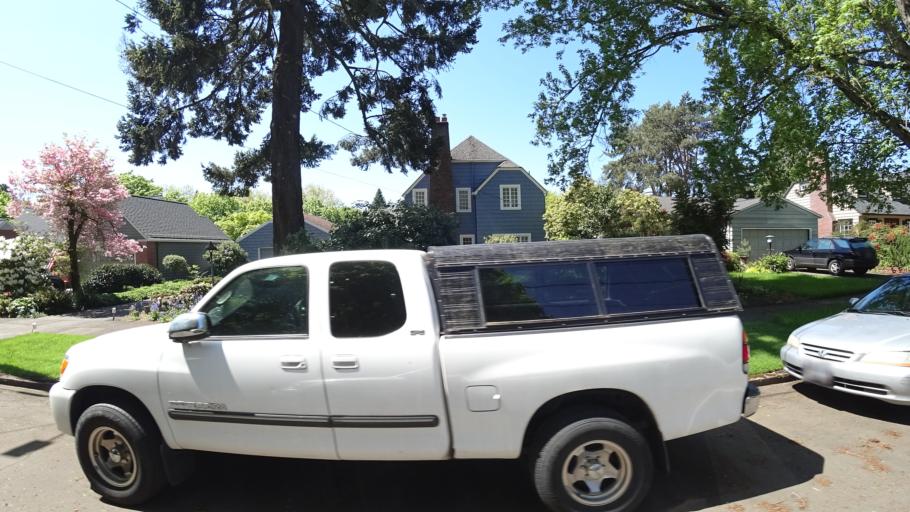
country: US
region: Oregon
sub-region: Clackamas County
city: Milwaukie
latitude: 45.4676
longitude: -122.6345
